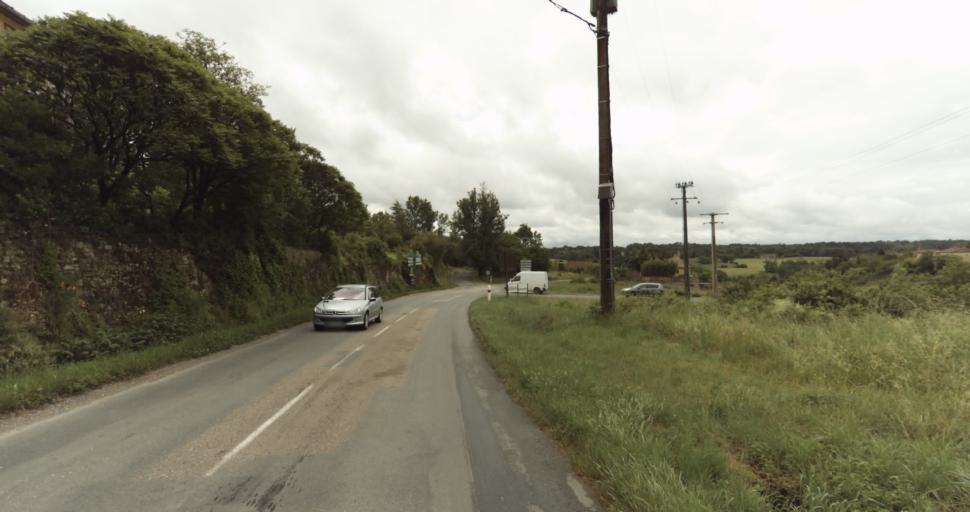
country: FR
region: Aquitaine
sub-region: Departement de la Dordogne
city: Belves
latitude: 44.6816
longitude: 0.8978
